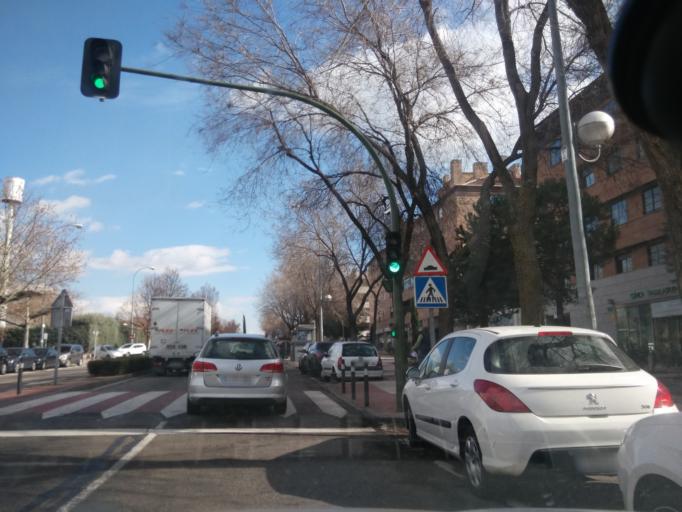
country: ES
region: Madrid
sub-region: Provincia de Madrid
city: Alcobendas
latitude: 40.5467
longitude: -3.6539
